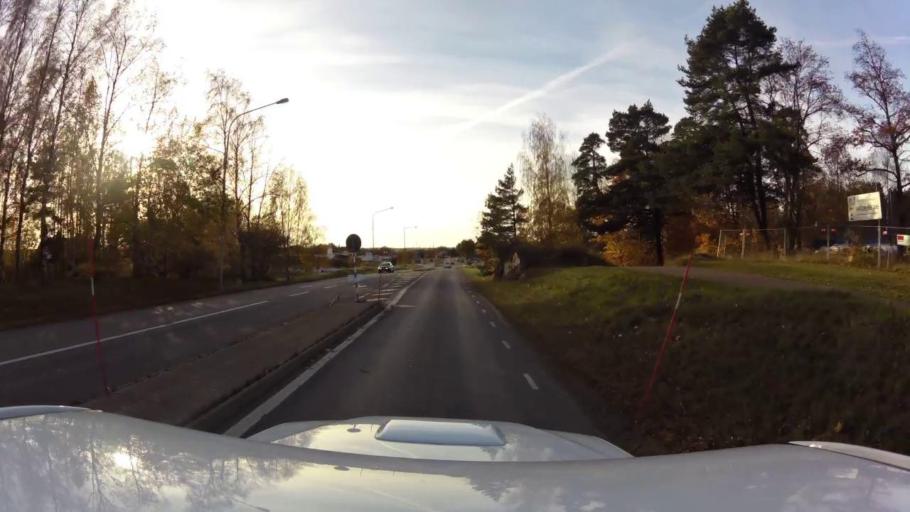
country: SE
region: OEstergoetland
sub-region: Linkopings Kommun
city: Linkoping
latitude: 58.4262
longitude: 15.6824
